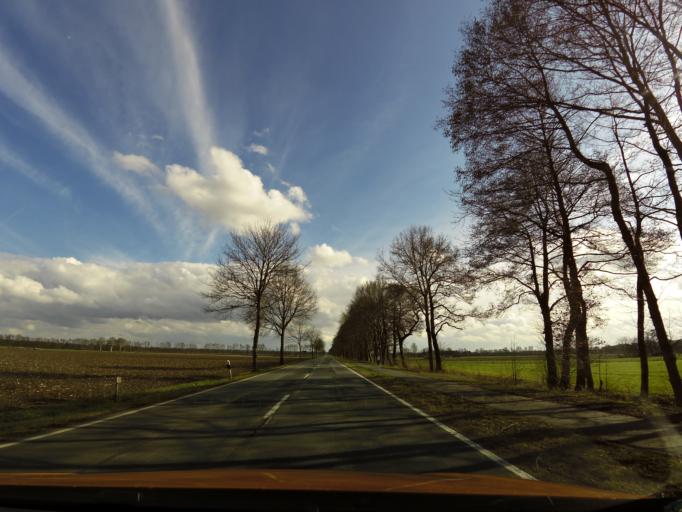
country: DE
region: Lower Saxony
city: Hatten
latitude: 53.0556
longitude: 8.3167
